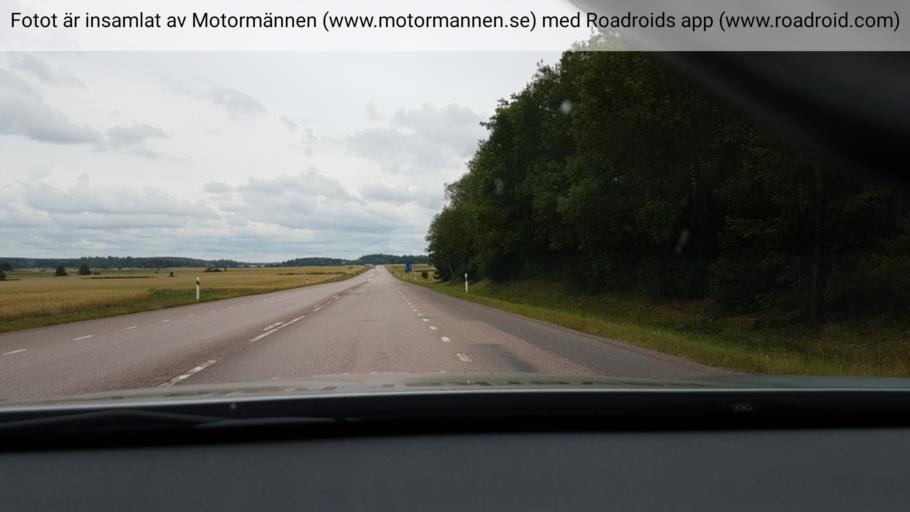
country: SE
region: Uppsala
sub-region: Knivsta Kommun
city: Knivsta
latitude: 59.7511
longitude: 17.9045
